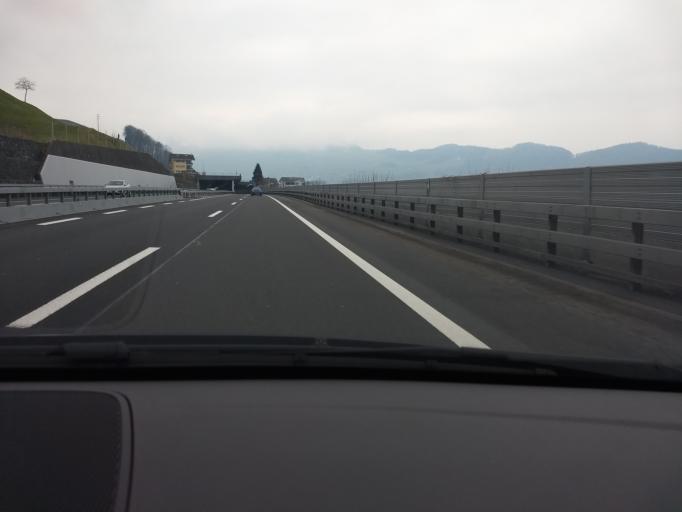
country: CH
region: Nidwalden
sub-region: Nidwalden
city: Beckenried
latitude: 46.9655
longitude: 8.4644
